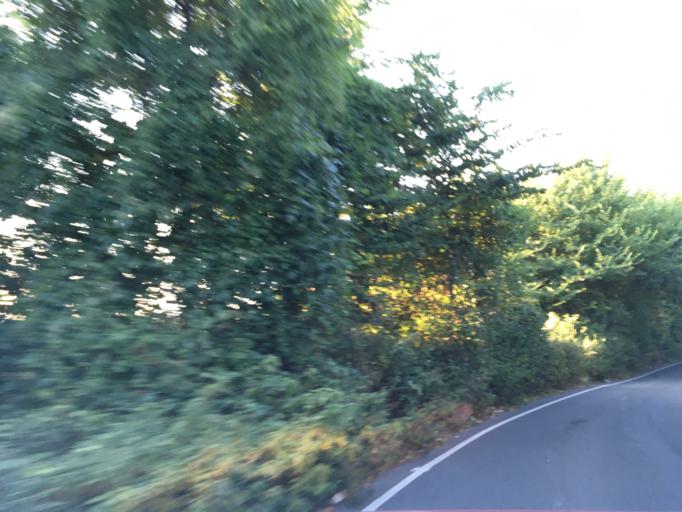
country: GB
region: England
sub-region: Bath and North East Somerset
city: Whitchurch
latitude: 51.4178
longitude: -2.5344
